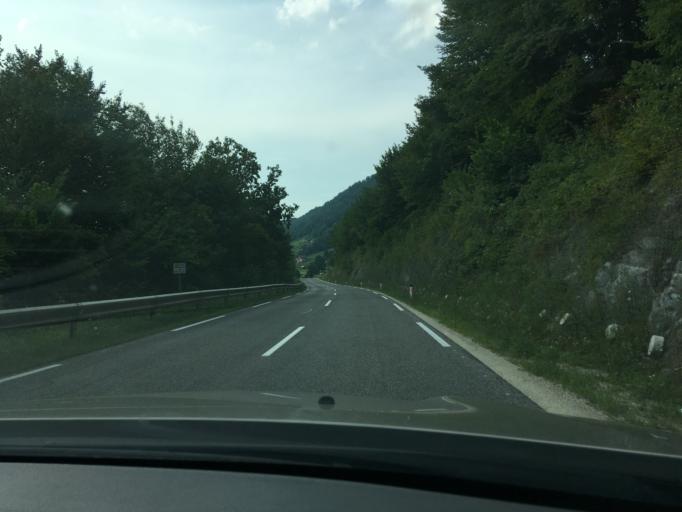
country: SI
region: Zuzemberk
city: Zuzemberk
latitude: 45.7919
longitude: 14.9884
